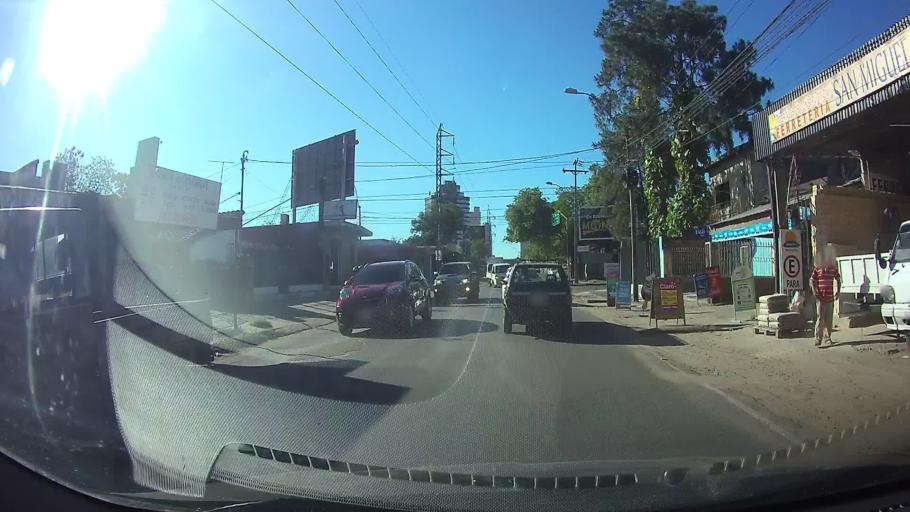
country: PY
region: Central
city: Fernando de la Mora
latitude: -25.2952
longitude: -57.5483
